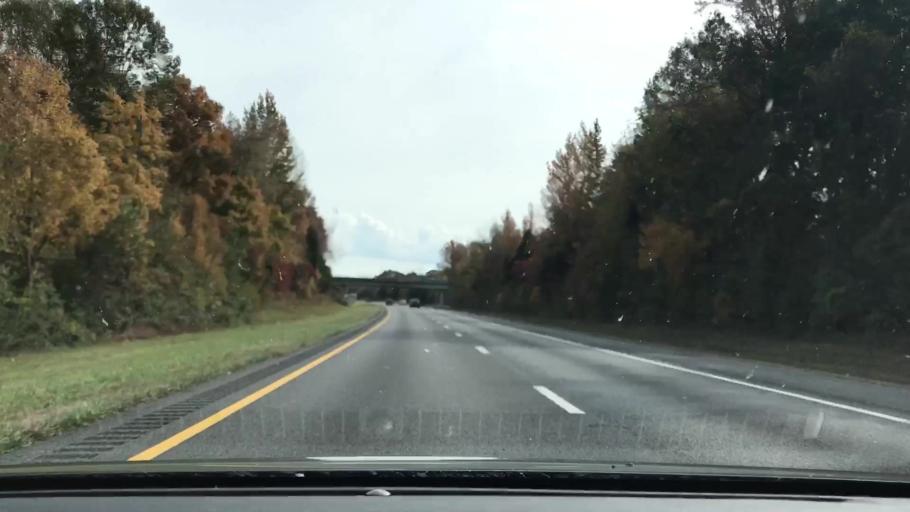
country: US
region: Kentucky
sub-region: Todd County
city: Guthrie
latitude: 36.5157
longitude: -87.2099
